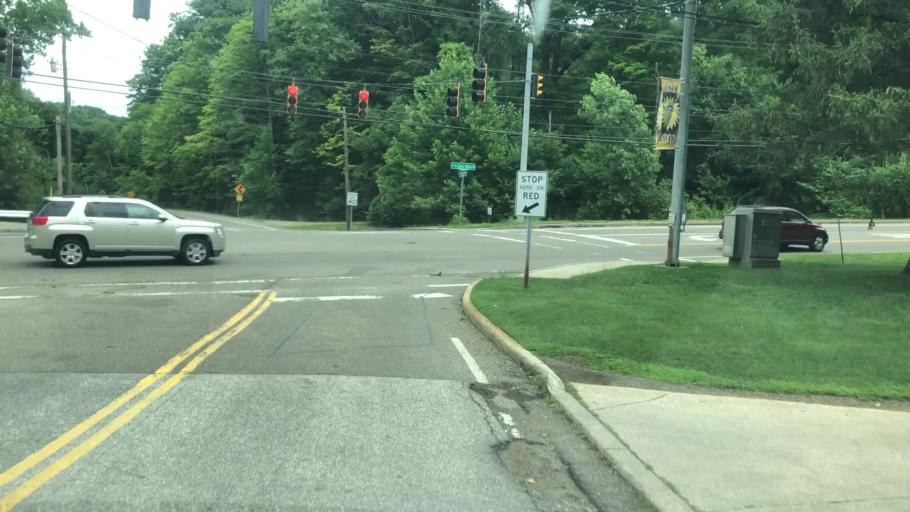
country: US
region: Ohio
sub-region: Summit County
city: Montrose-Ghent
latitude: 41.1568
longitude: -81.6355
